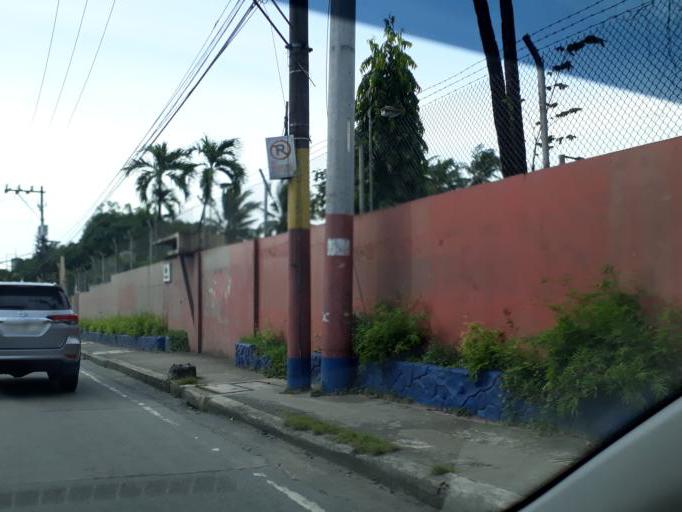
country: PH
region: Metro Manila
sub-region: Caloocan City
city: Niugan
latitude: 14.6697
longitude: 120.9753
